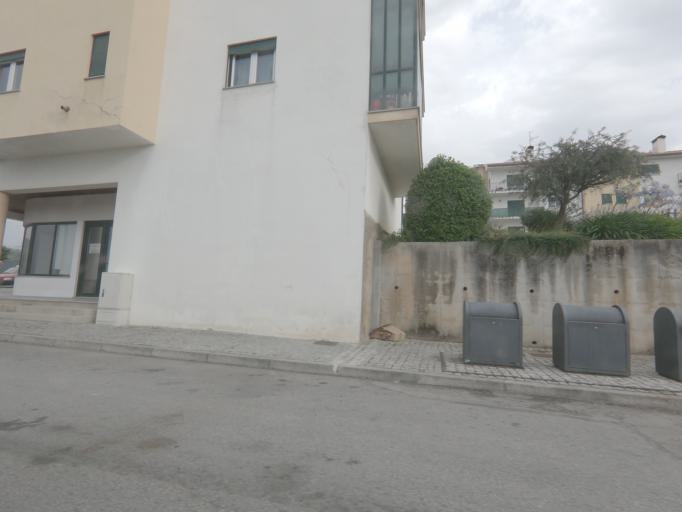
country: PT
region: Viseu
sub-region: Armamar
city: Armamar
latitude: 41.1093
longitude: -7.6894
